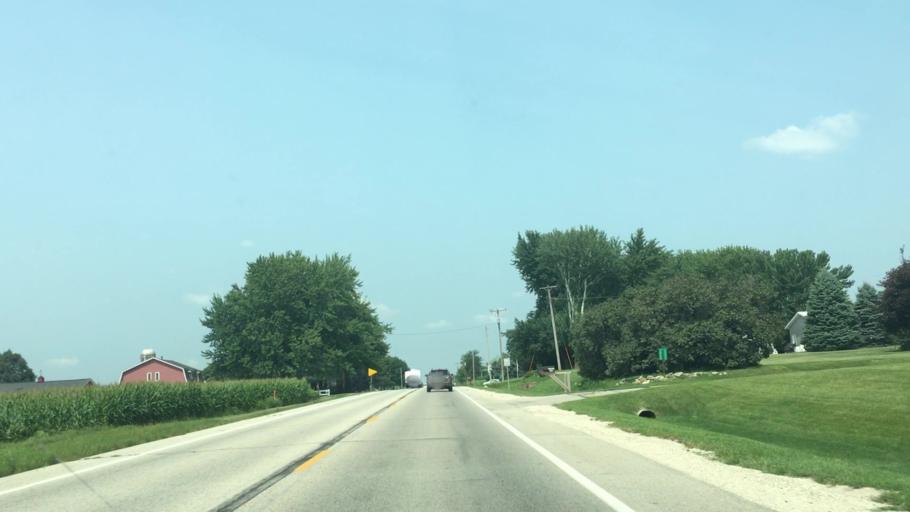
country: US
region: Iowa
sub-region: Buchanan County
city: Independence
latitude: 42.4859
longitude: -91.8894
